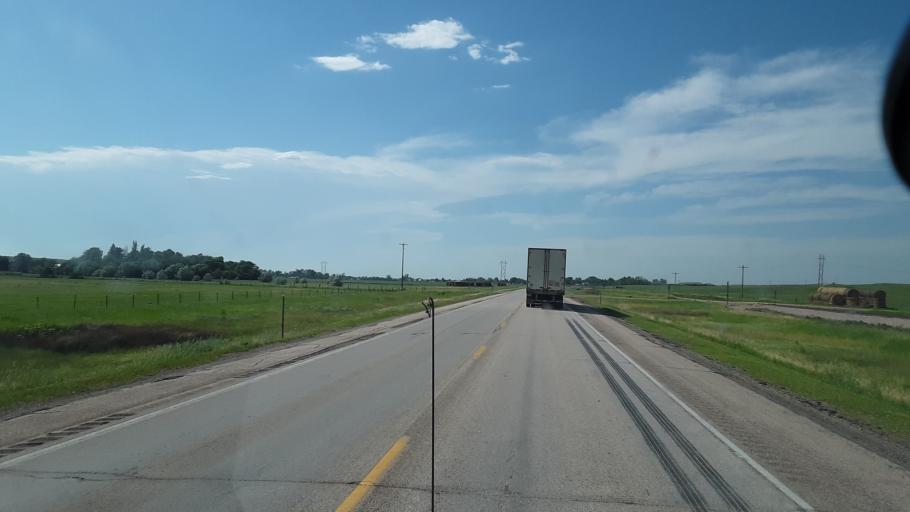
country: US
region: South Dakota
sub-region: Lawrence County
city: Deadwood
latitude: 44.5306
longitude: -103.7045
